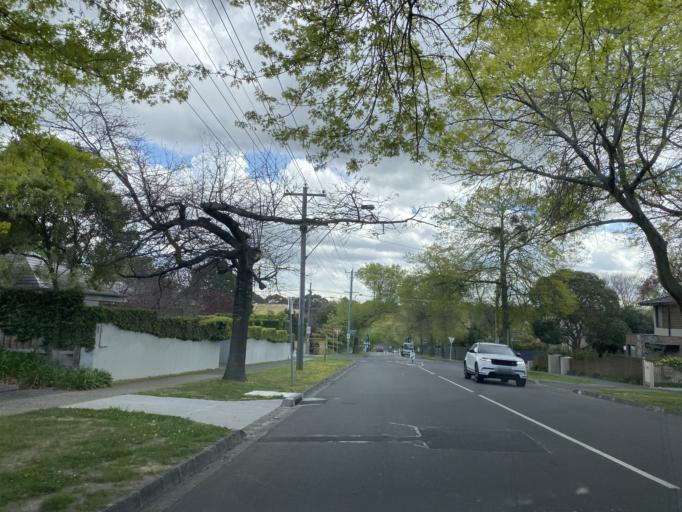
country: AU
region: Victoria
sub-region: Boroondara
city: Canterbury
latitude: -37.8302
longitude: 145.0750
